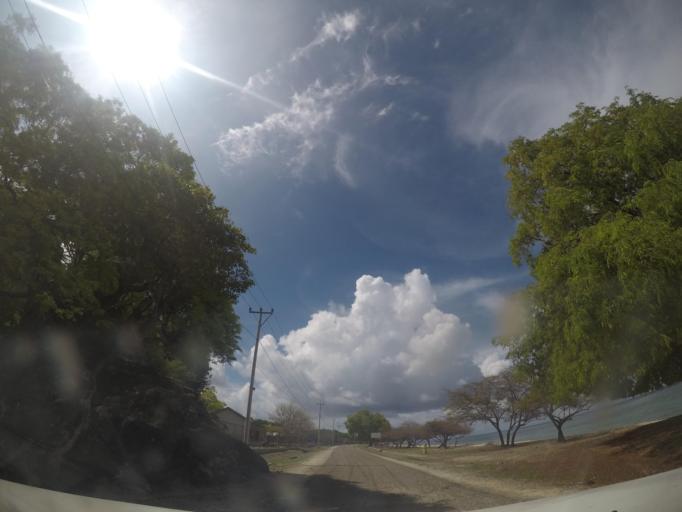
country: TL
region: Lautem
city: Lospalos
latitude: -8.3516
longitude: 127.0529
